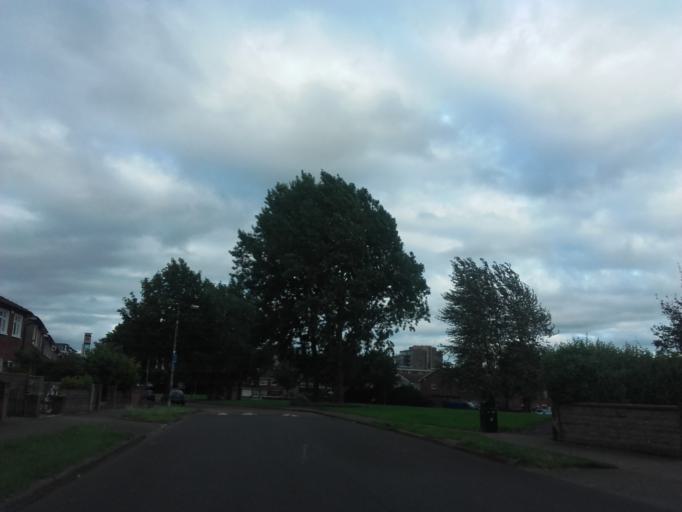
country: IE
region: Leinster
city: Tallaght
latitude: 53.2871
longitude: -6.3816
